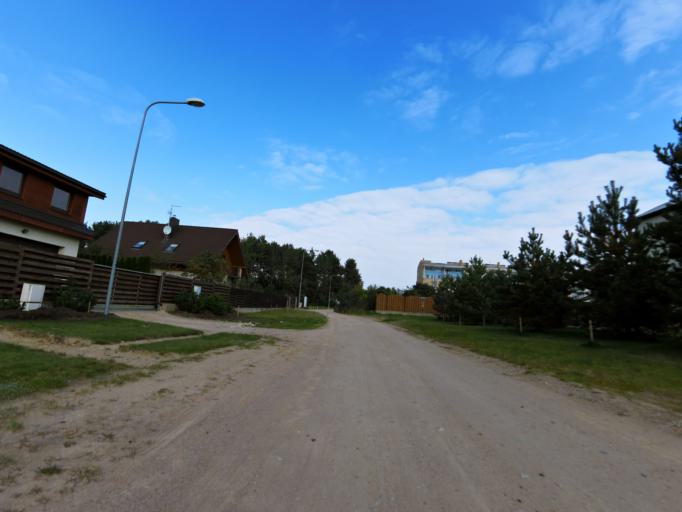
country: LT
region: Vilnius County
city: Pilaite
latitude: 54.7015
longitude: 25.1656
